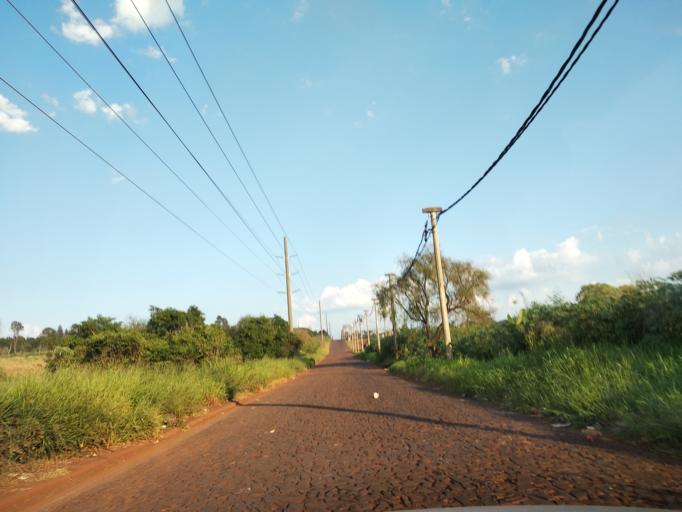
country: AR
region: Misiones
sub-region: Departamento de Capital
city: Posadas
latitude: -27.4426
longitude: -55.9382
